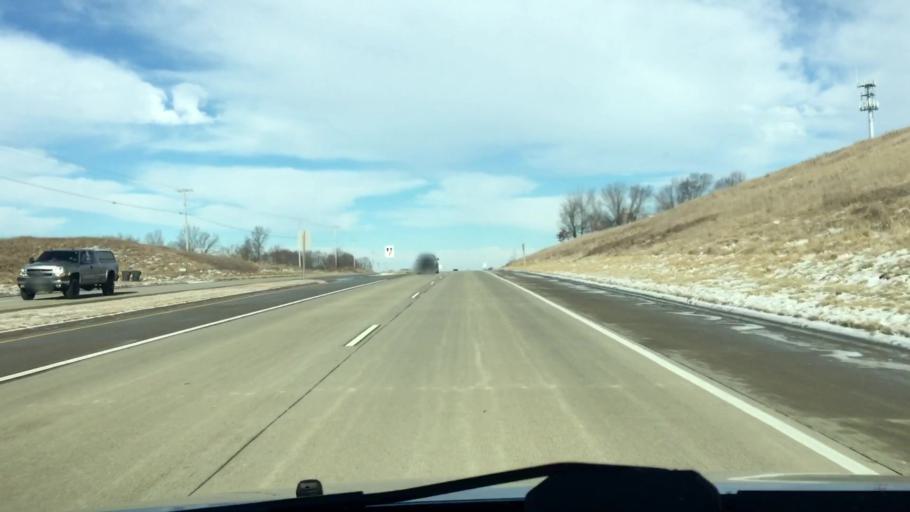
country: US
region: Wisconsin
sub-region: Waukesha County
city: Mukwonago
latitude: 42.9074
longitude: -88.3454
